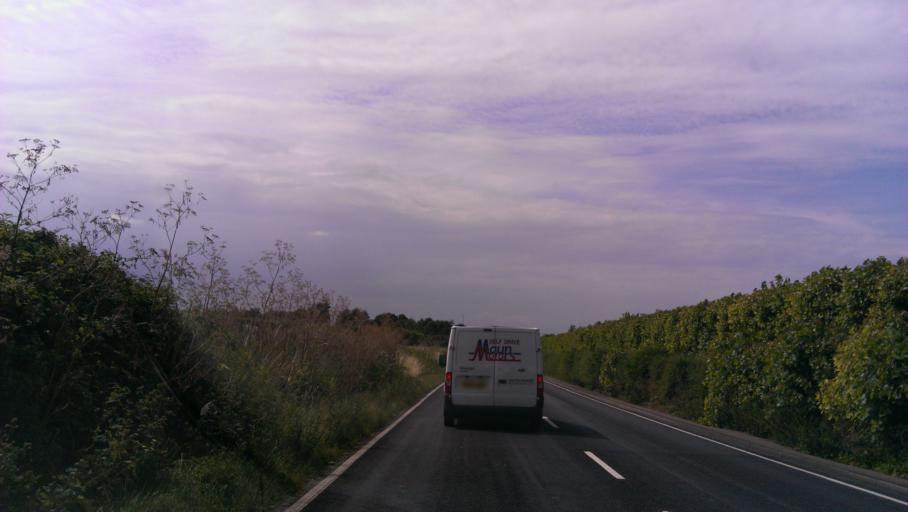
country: GB
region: England
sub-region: Kent
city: Teynham
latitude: 51.3183
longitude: 0.8396
